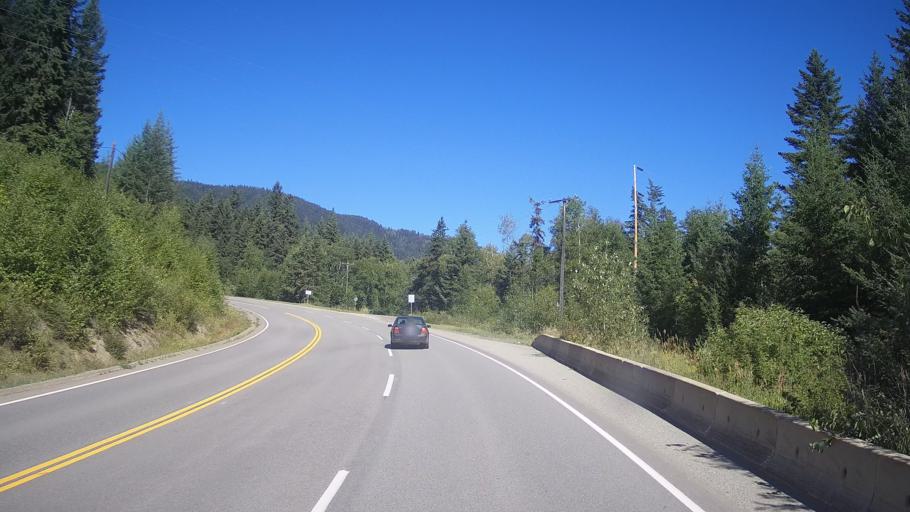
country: CA
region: British Columbia
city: Kamloops
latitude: 51.4663
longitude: -120.2345
